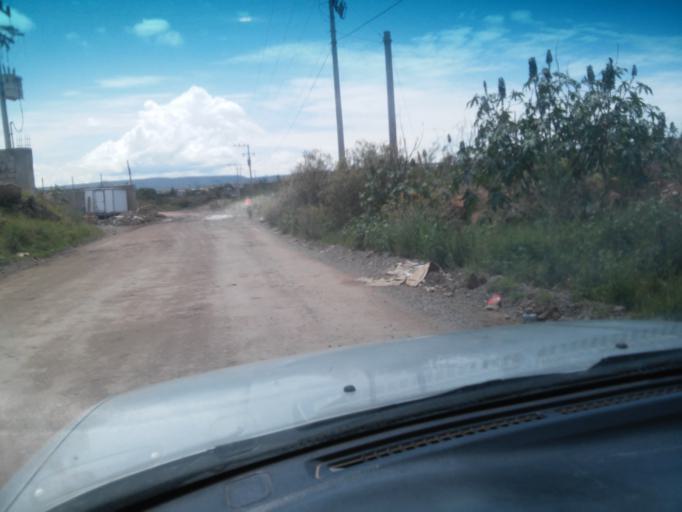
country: MX
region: Durango
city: Victoria de Durango
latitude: 23.9890
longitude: -104.7109
